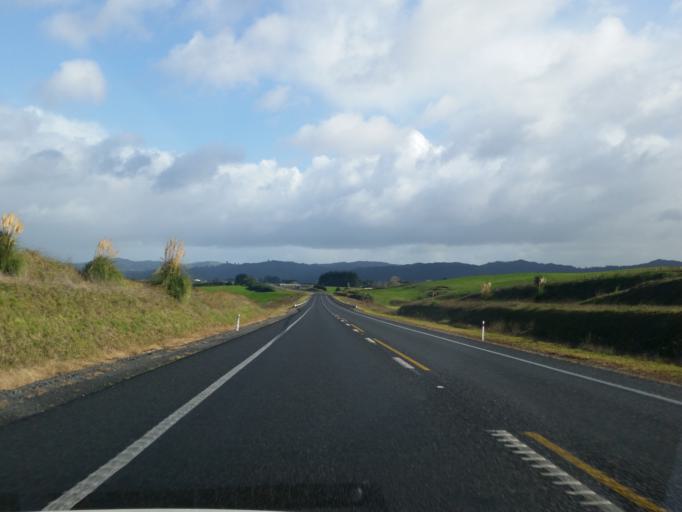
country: NZ
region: Waikato
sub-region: Waikato District
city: Te Kauwhata
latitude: -37.2254
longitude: 175.1511
